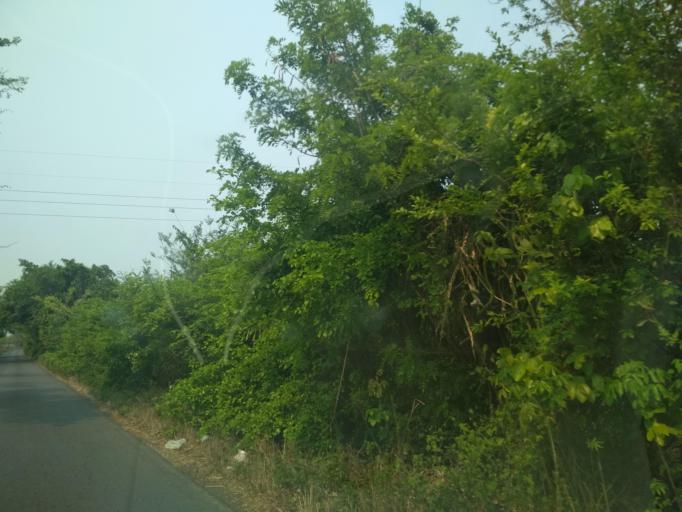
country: MX
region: Veracruz
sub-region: Veracruz
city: Delfino Victoria (Santa Fe)
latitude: 19.2117
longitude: -96.3122
